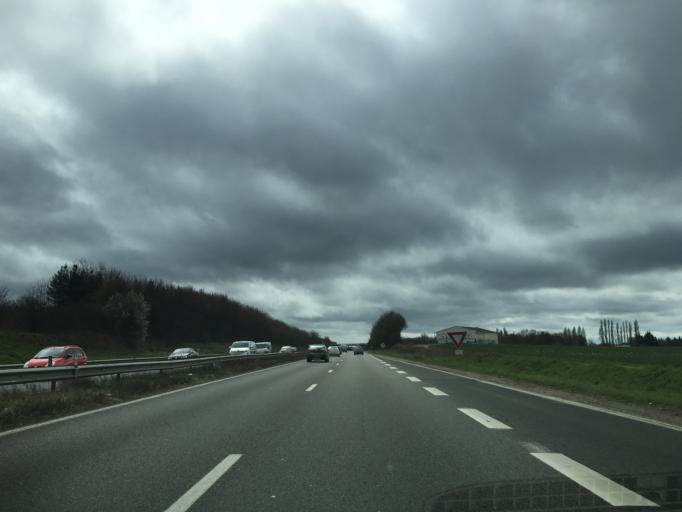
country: FR
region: Ile-de-France
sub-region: Departement de Seine-et-Marne
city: Servon
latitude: 48.6981
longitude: 2.5941
